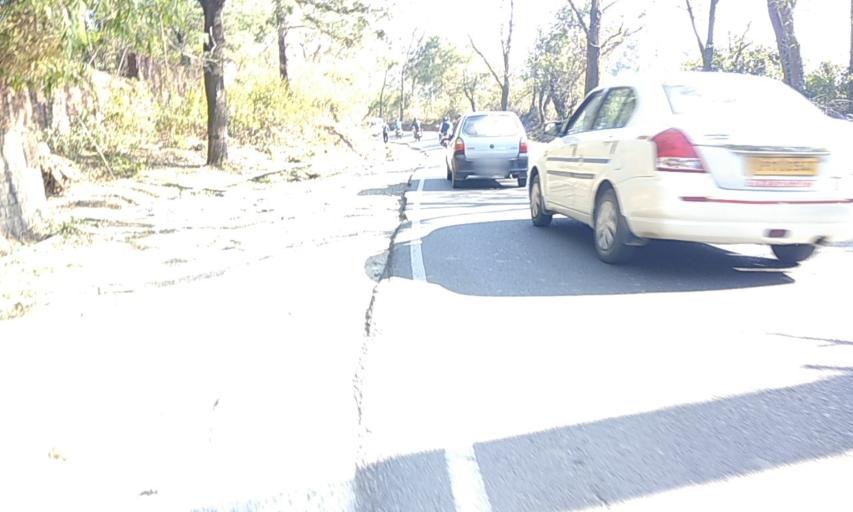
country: IN
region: Himachal Pradesh
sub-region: Kangra
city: Palampur
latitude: 32.1039
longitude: 76.5549
